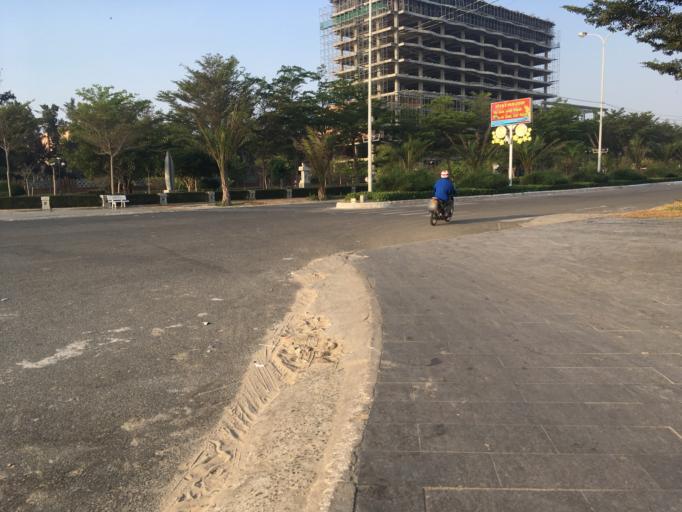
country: VN
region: Ninh Thuan
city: Khanh Hai
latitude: 11.5628
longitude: 109.0243
